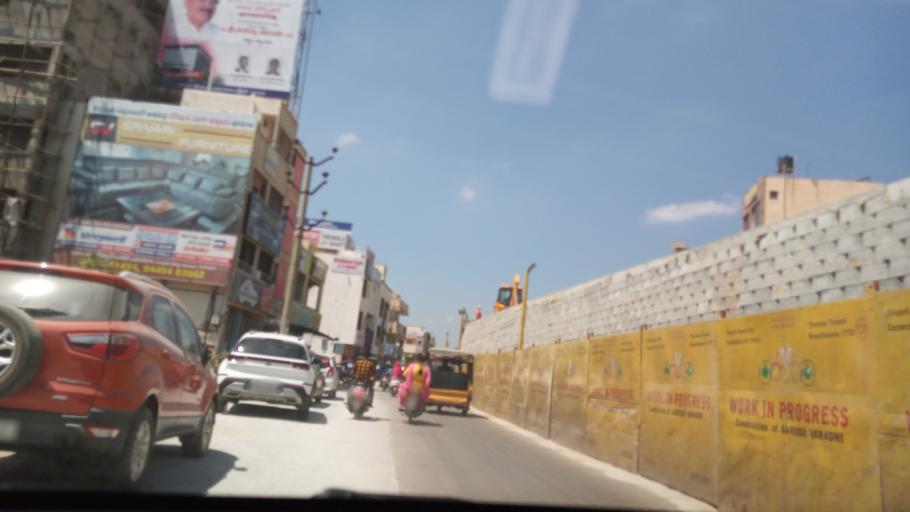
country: IN
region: Andhra Pradesh
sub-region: Chittoor
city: Akkarampalle
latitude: 13.6430
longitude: 79.4330
